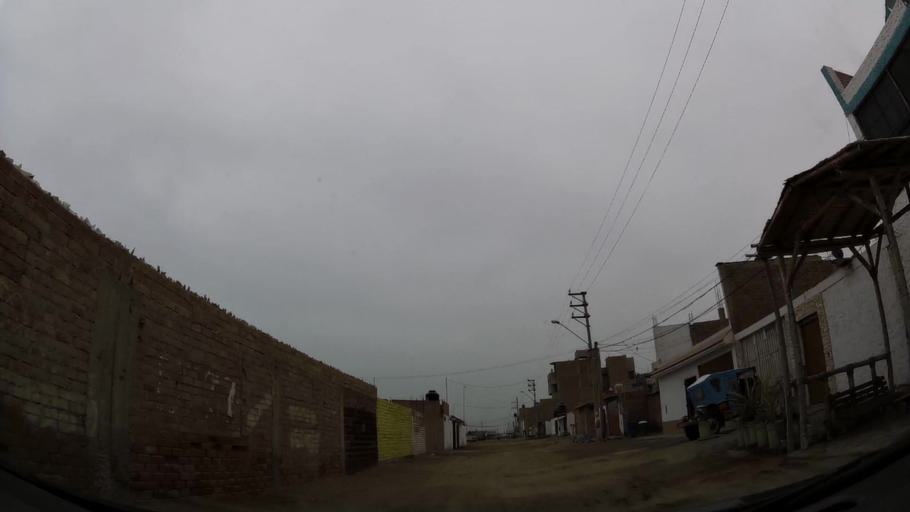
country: PE
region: Lima
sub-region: Lima
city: Punta Hermosa
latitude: -12.3308
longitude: -76.8234
